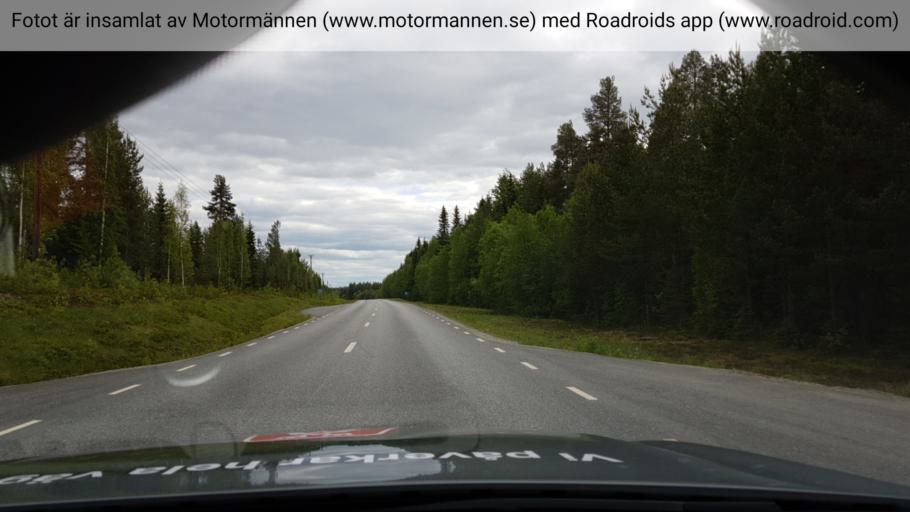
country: SE
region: Jaemtland
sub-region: Stroemsunds Kommun
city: Stroemsund
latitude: 63.9526
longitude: 15.4824
